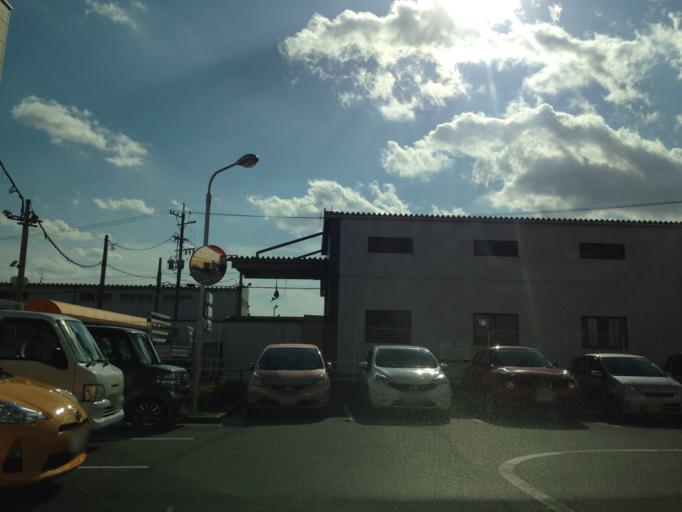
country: JP
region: Shizuoka
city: Fukuroi
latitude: 34.7490
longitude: 137.9085
